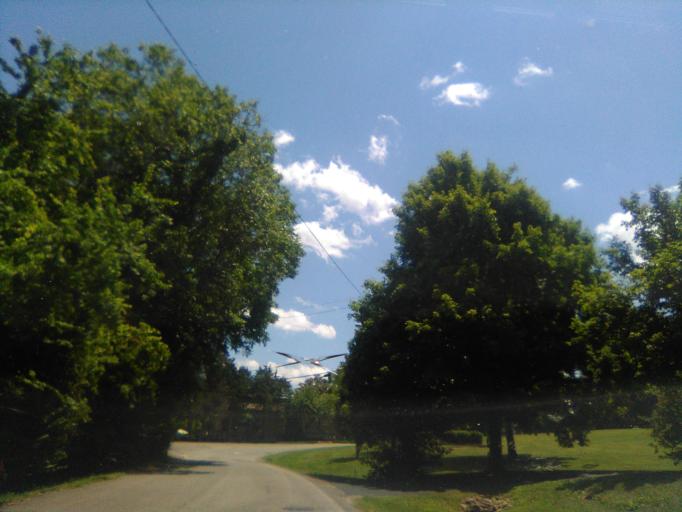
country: US
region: Tennessee
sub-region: Davidson County
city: Belle Meade
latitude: 36.1256
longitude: -86.8701
